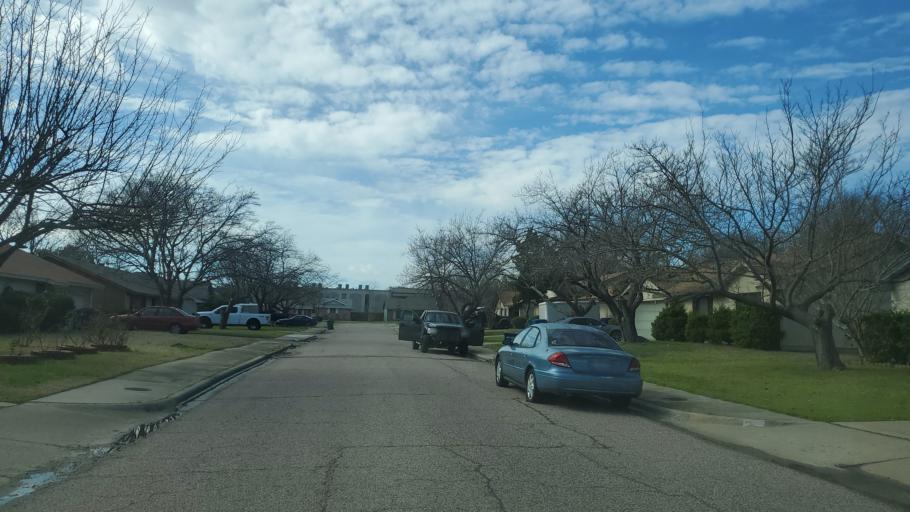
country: US
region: Texas
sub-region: Dallas County
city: Carrollton
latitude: 32.9800
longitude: -96.8870
